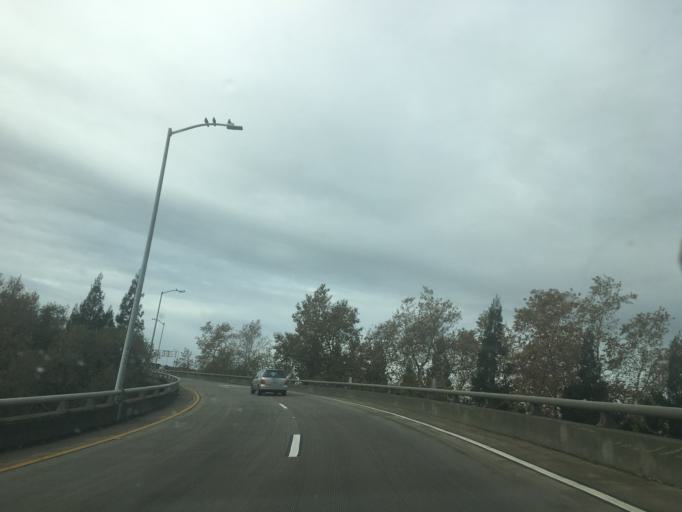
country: US
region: California
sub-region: Sacramento County
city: Sacramento
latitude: 38.5696
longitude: -121.5073
